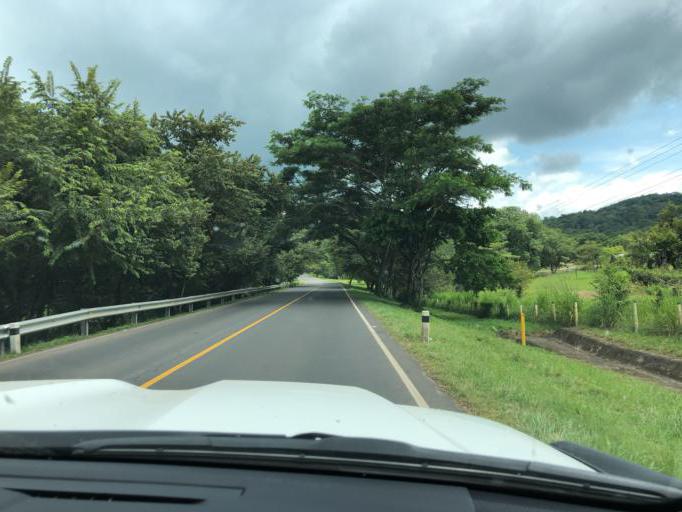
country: NI
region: Chontales
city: Villa Sandino
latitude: 12.0545
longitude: -85.0328
